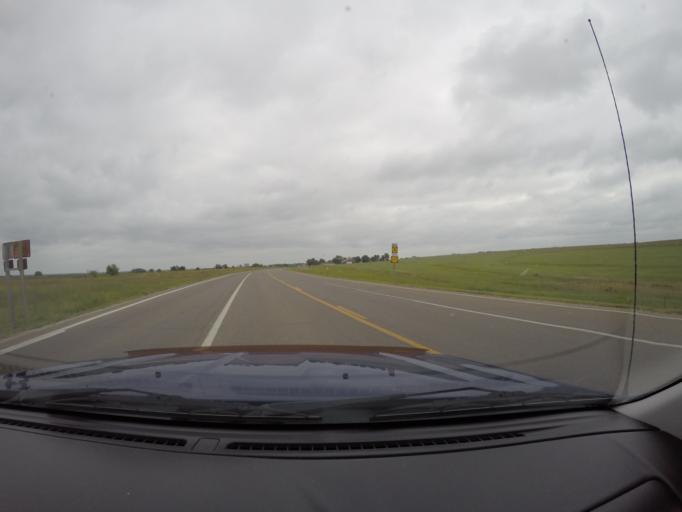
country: US
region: Kansas
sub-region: Morris County
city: Council Grove
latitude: 38.8551
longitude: -96.5017
